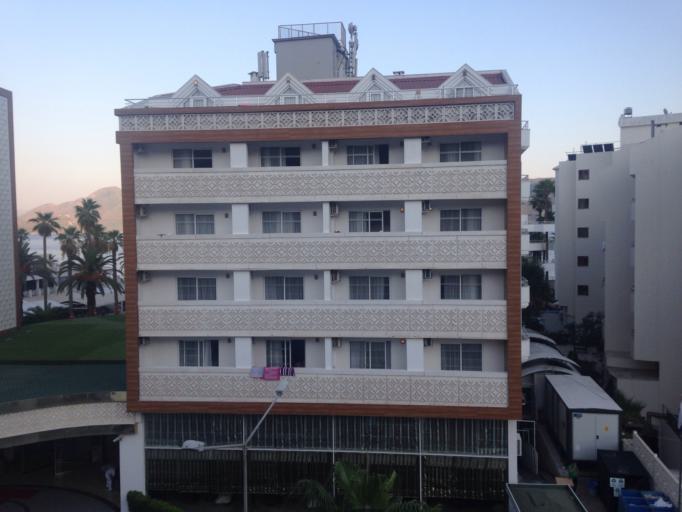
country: TR
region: Mugla
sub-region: Marmaris
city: Marmaris
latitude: 36.8339
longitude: 28.2448
